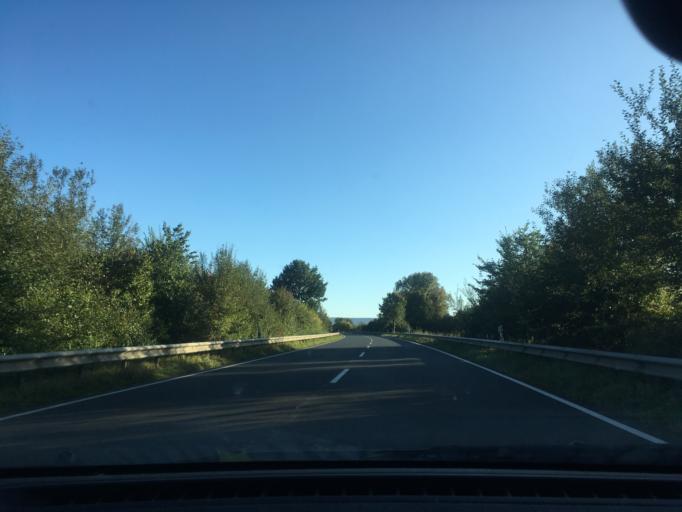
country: DE
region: Lower Saxony
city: Einbeck
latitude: 51.8305
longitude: 9.8308
